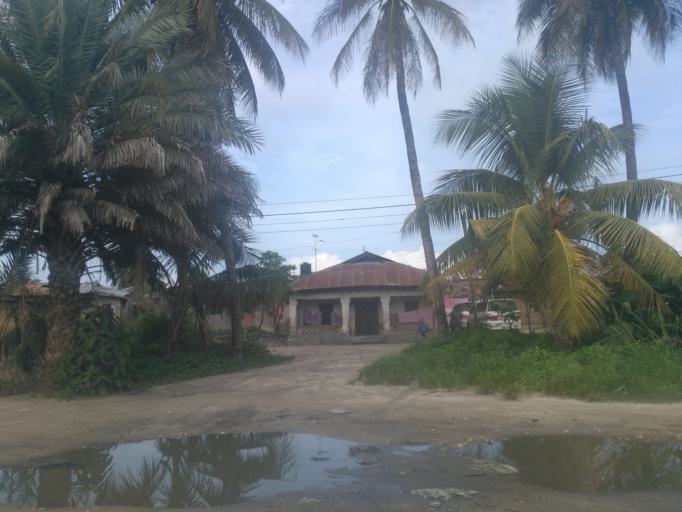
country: TZ
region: Zanzibar Urban/West
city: Zanzibar
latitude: -6.1680
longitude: 39.2026
